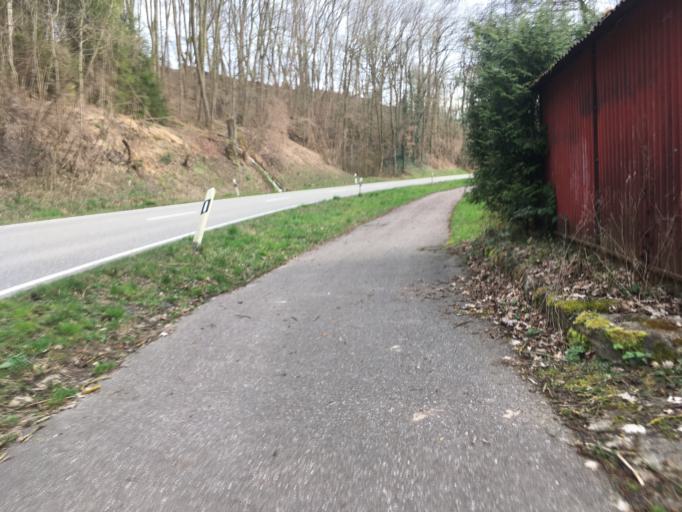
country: DE
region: Baden-Wuerttemberg
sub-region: Regierungsbezirk Stuttgart
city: Bretzfeld
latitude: 49.2102
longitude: 9.4239
